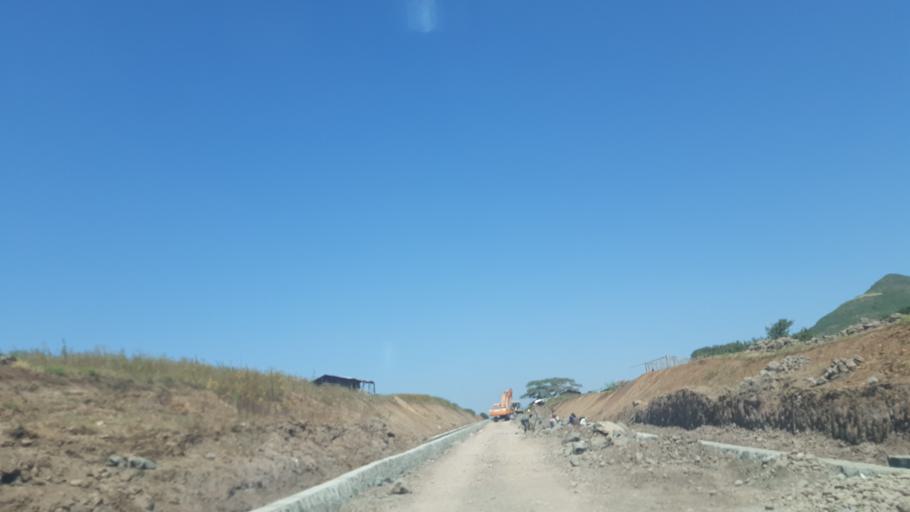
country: ET
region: Amhara
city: Dabat
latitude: 13.1608
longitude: 37.6073
